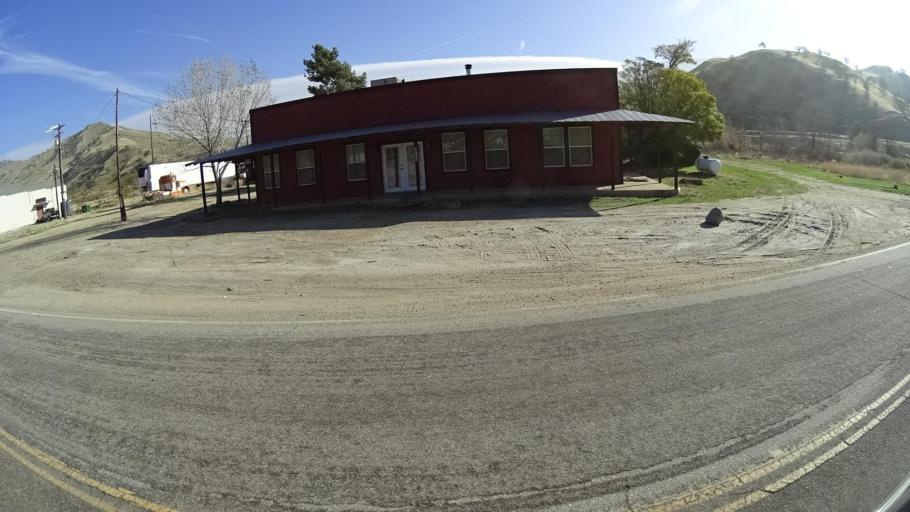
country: US
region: California
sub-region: Kern County
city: Bear Valley Springs
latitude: 35.2899
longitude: -118.6283
